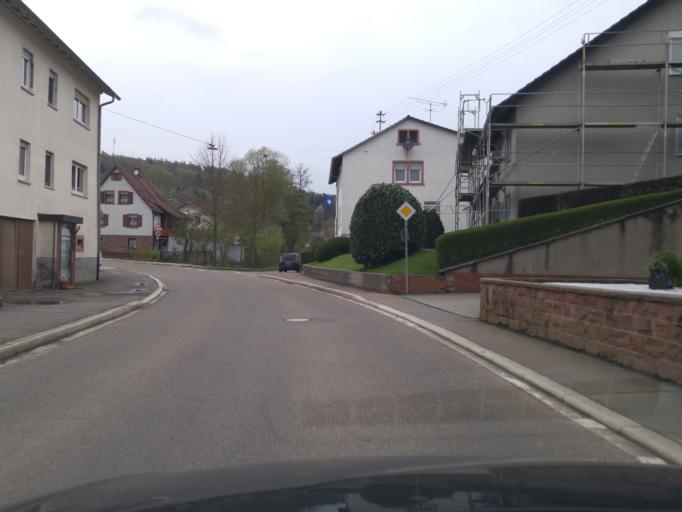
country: DE
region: Baden-Wuerttemberg
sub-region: Karlsruhe Region
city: Reichartshausen
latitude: 49.3735
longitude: 8.9644
